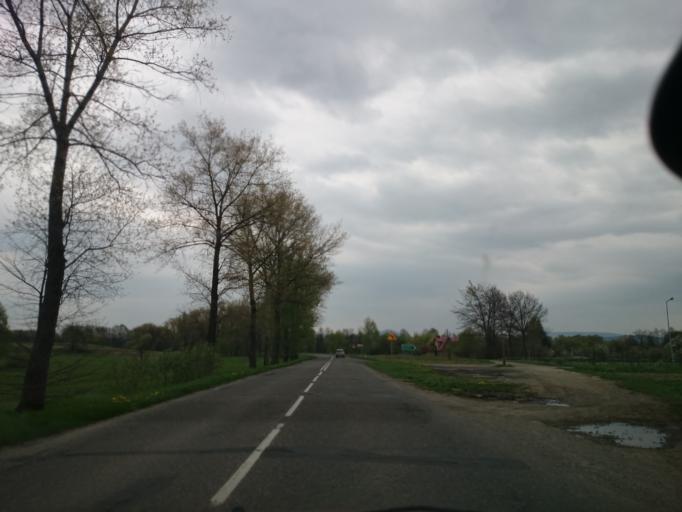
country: PL
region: Opole Voivodeship
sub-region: Powiat nyski
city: Glucholazy
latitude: 50.3701
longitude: 17.3630
